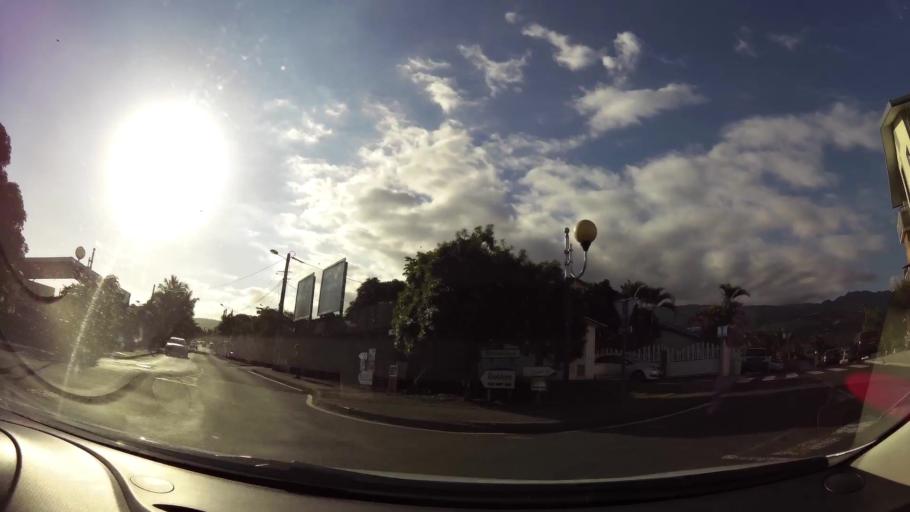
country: RE
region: Reunion
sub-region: Reunion
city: Les Avirons
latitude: -21.2706
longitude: 55.3695
